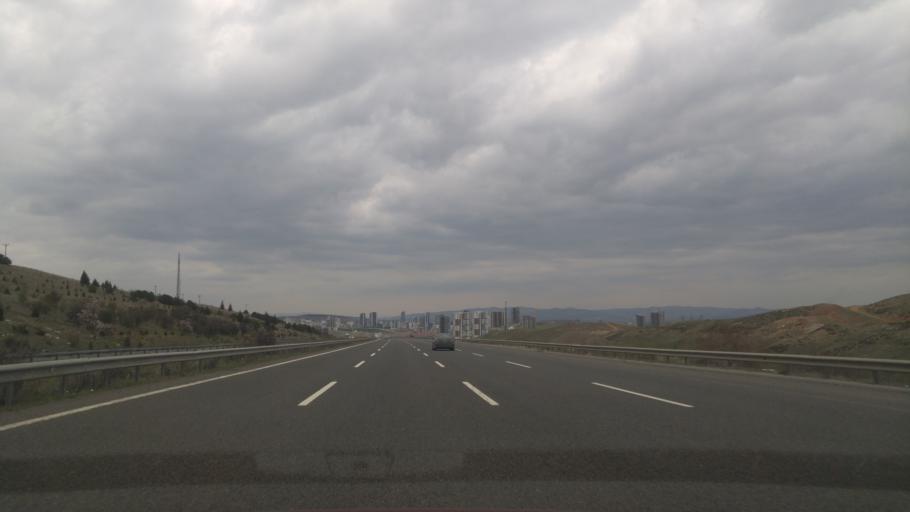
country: TR
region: Ankara
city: Etimesgut
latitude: 39.8188
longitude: 32.6460
